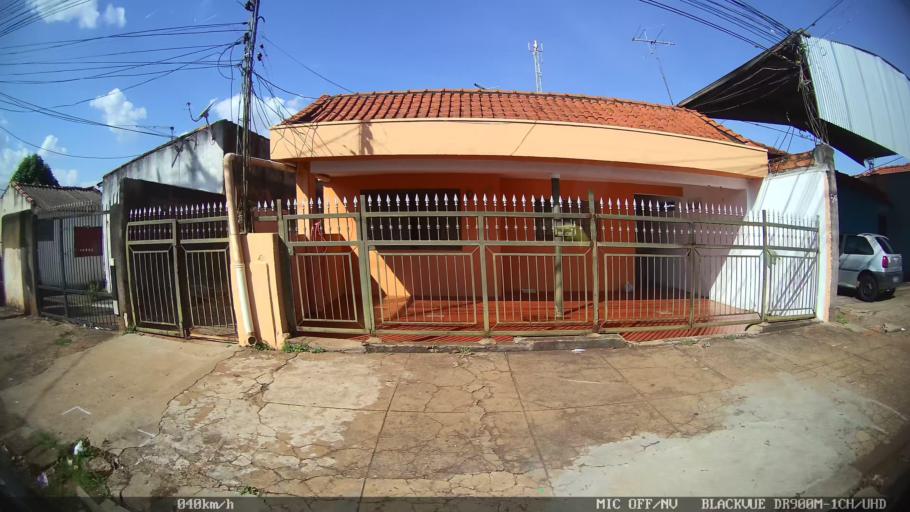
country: BR
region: Sao Paulo
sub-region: Ribeirao Preto
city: Ribeirao Preto
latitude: -21.1869
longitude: -47.8249
